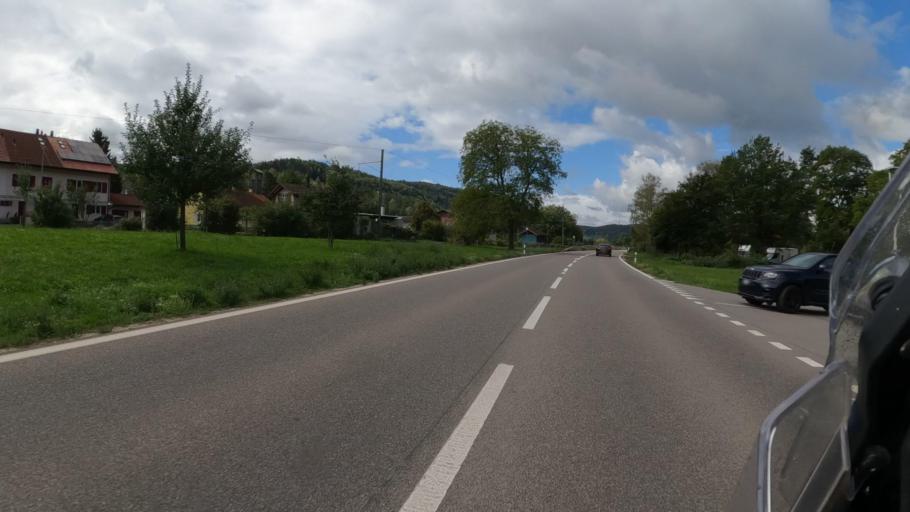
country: CH
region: Aargau
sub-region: Bezirk Zurzach
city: Bad Zurzach
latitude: 47.5687
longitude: 8.3539
